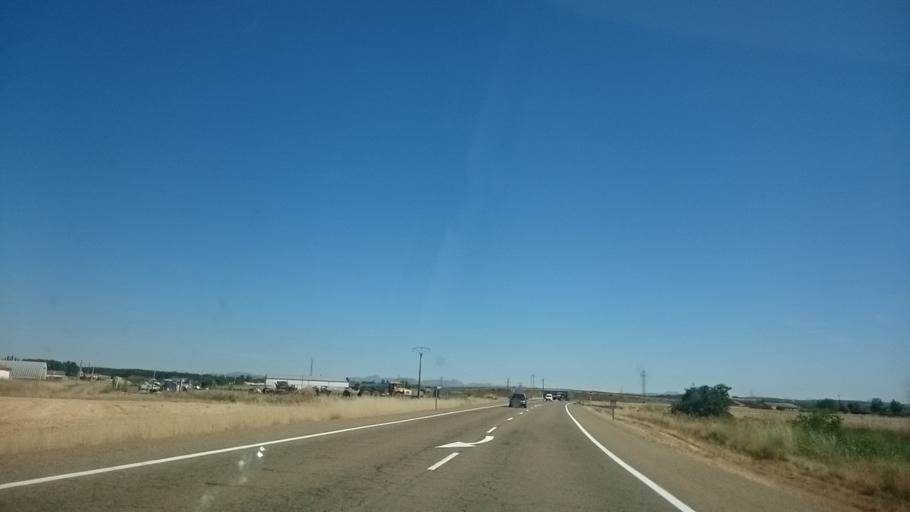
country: ES
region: Castille and Leon
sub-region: Provincia de Leon
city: Mansilla de las Mulas
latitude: 42.4894
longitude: -5.4081
